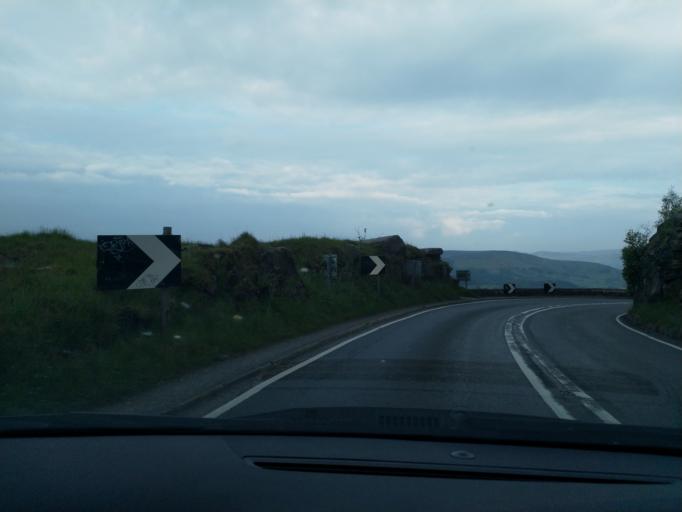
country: GB
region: England
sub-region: Derbyshire
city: Hathersage
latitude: 53.3162
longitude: -1.6277
